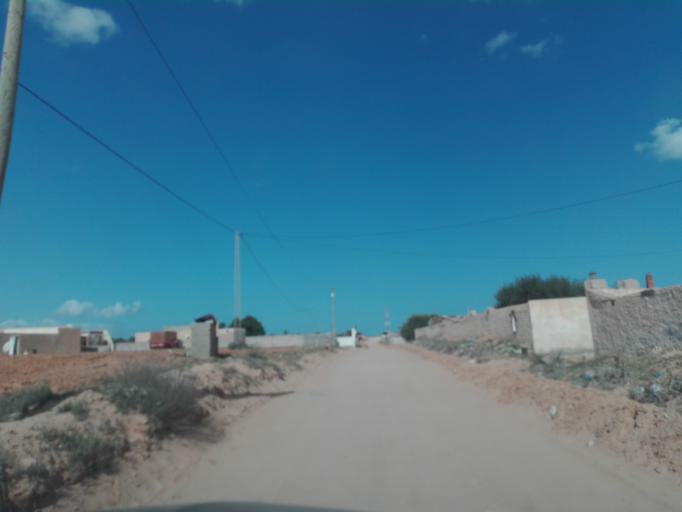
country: TN
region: Madanin
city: Bin Qirdan
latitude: 33.1622
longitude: 11.1954
